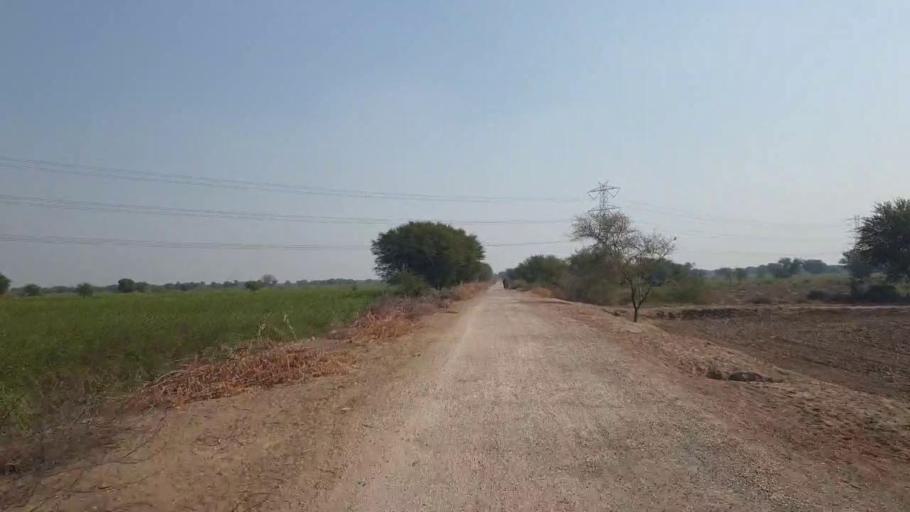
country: PK
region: Sindh
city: Chambar
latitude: 25.3520
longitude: 68.9190
